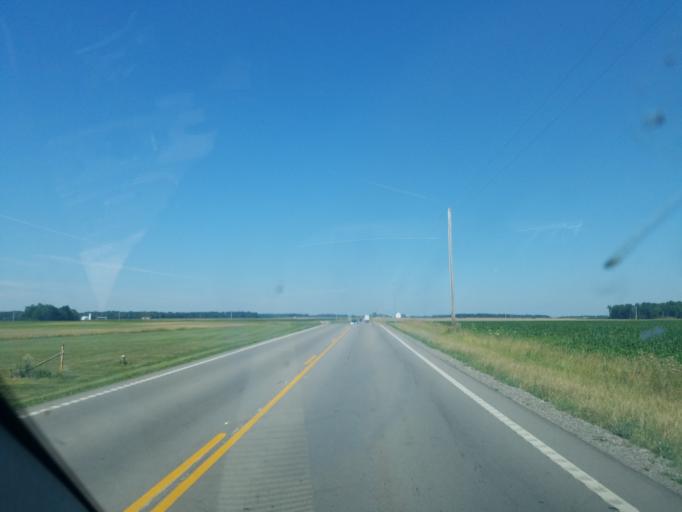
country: US
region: Ohio
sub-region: Logan County
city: Lakeview
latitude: 40.4393
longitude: -83.9608
